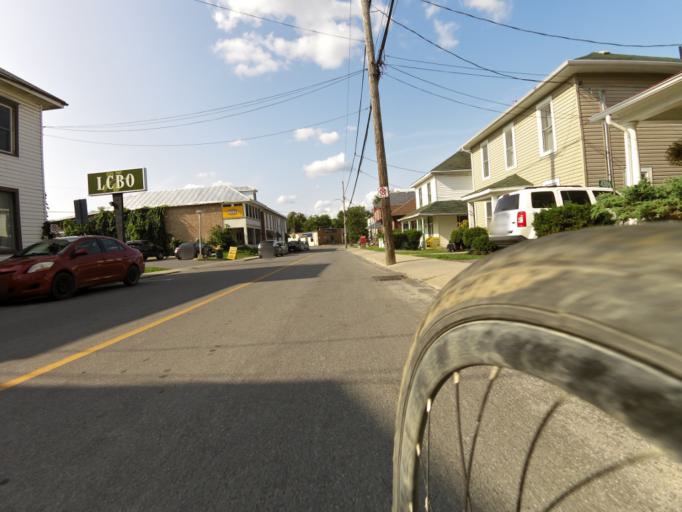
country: CA
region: Ontario
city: Kingston
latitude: 44.4101
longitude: -76.5966
